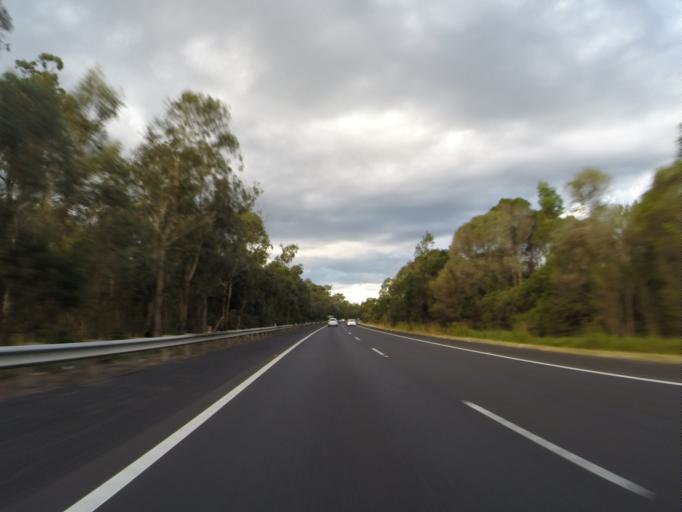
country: AU
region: New South Wales
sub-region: Wollondilly
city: Buxton
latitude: -34.3017
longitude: 150.6089
